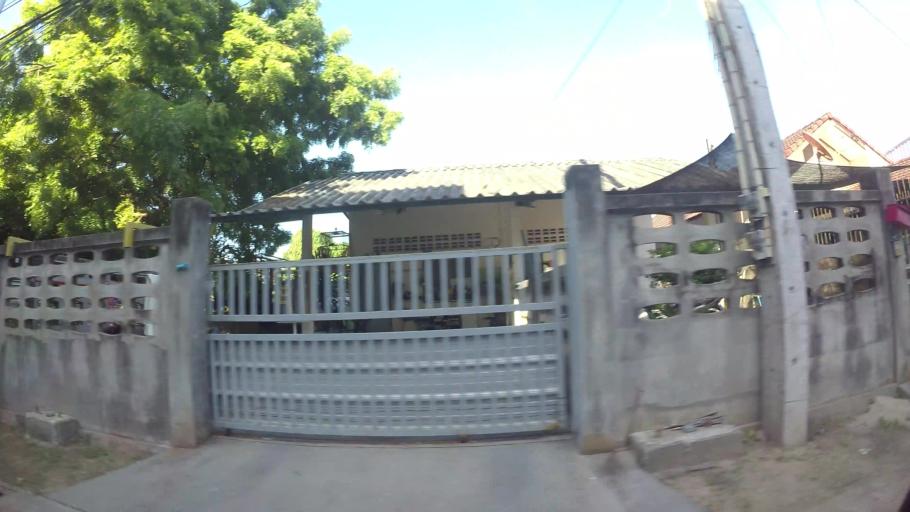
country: TH
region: Rayong
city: Rayong
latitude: 12.6656
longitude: 101.3005
